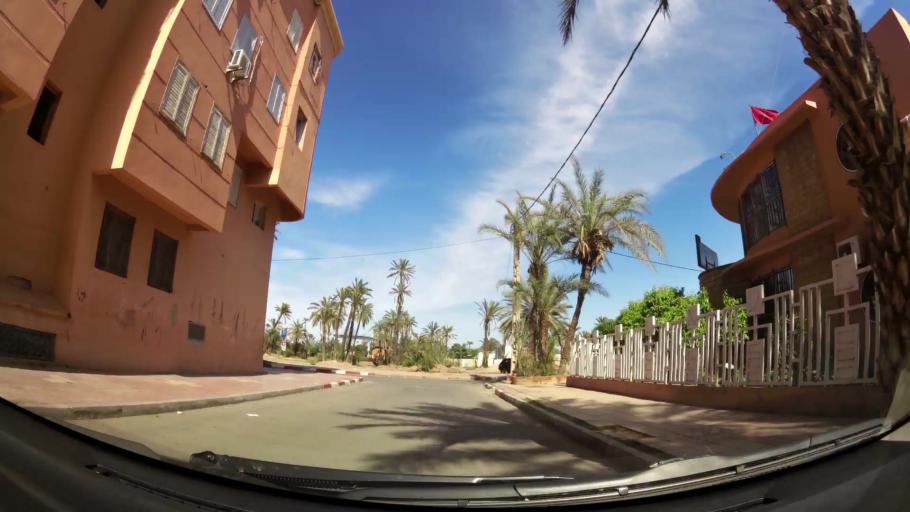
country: MA
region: Marrakech-Tensift-Al Haouz
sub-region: Marrakech
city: Marrakesh
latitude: 31.6452
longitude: -7.9785
